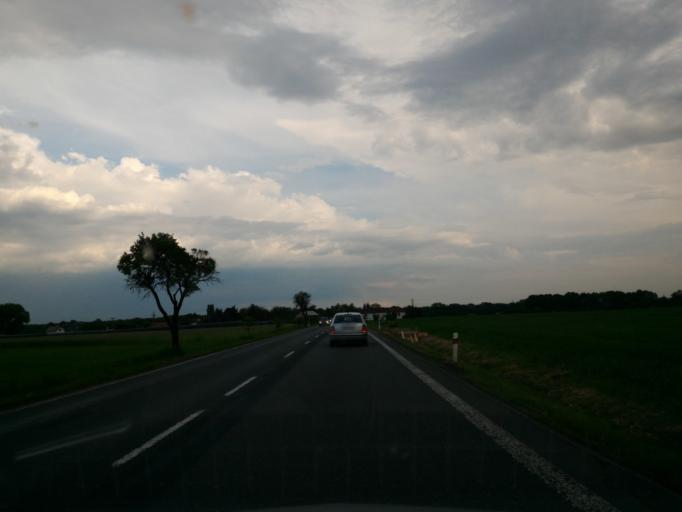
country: CZ
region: Central Bohemia
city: Libice nad Cidlinou
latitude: 50.1054
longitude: 15.1412
